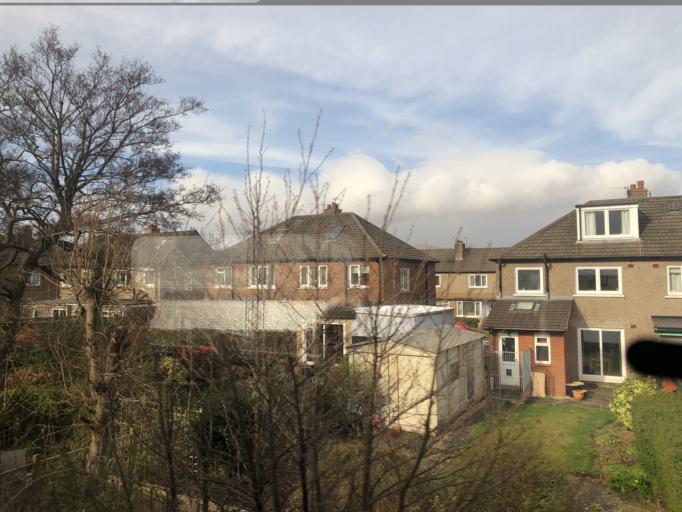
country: GB
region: Scotland
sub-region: Argyll and Bute
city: Helensburgh
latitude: 55.9944
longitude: -4.7084
